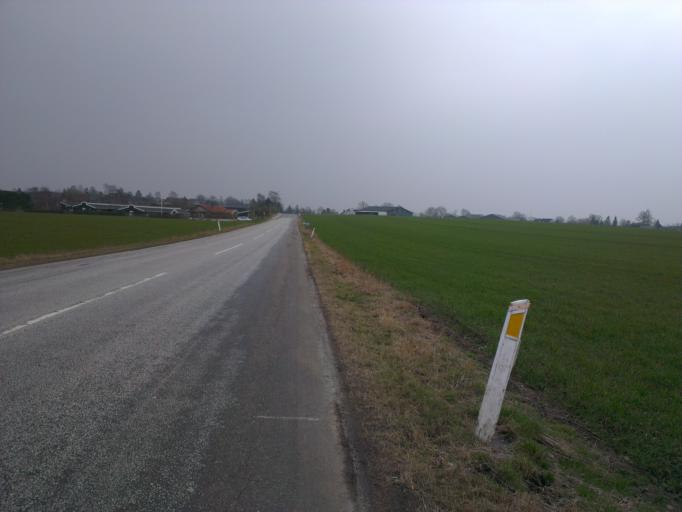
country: DK
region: Capital Region
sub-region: Egedal Kommune
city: Olstykke
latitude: 55.8027
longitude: 12.1114
